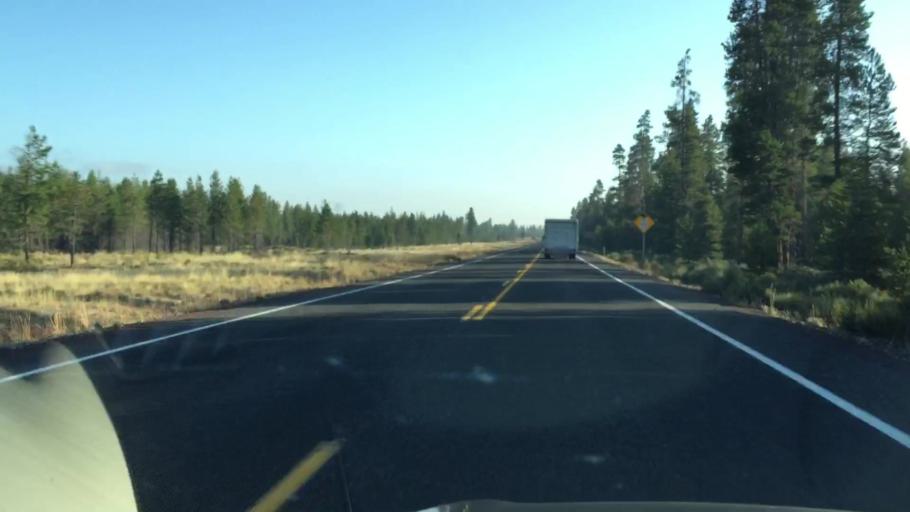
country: US
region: Oregon
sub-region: Deschutes County
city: La Pine
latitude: 43.4370
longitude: -121.7120
